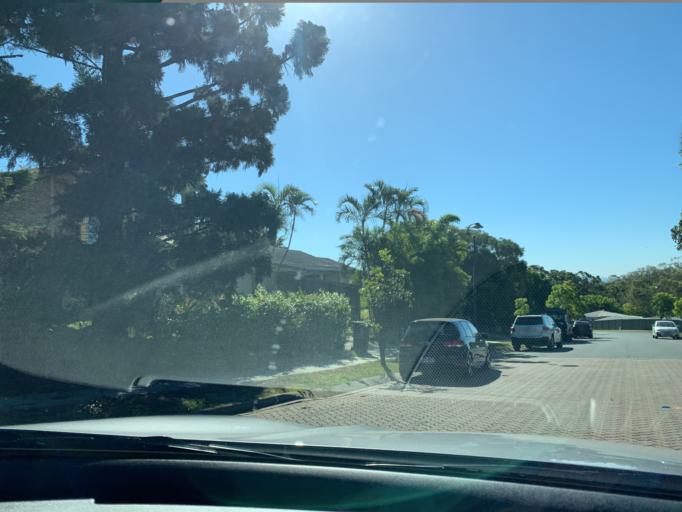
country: AU
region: Queensland
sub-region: Brisbane
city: Wynnum
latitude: -27.4280
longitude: 153.1631
